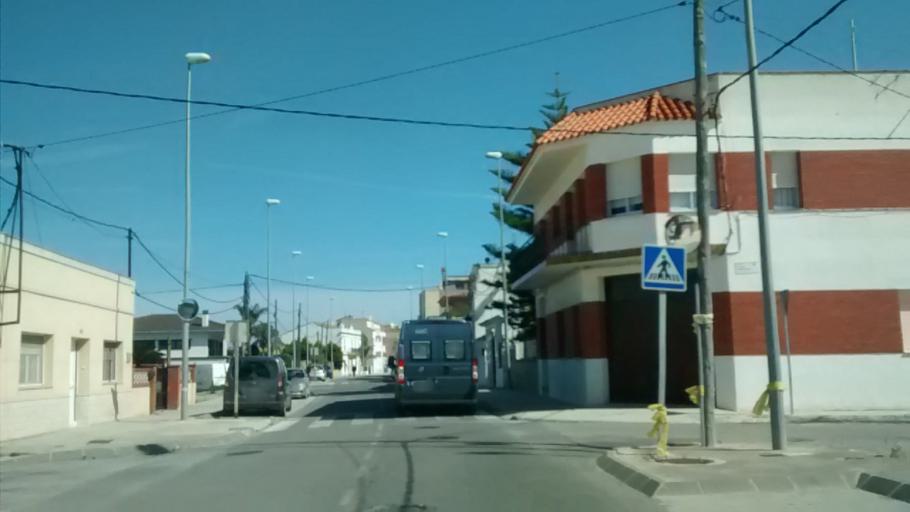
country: ES
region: Catalonia
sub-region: Provincia de Tarragona
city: Deltebre
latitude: 40.7152
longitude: 0.7469
